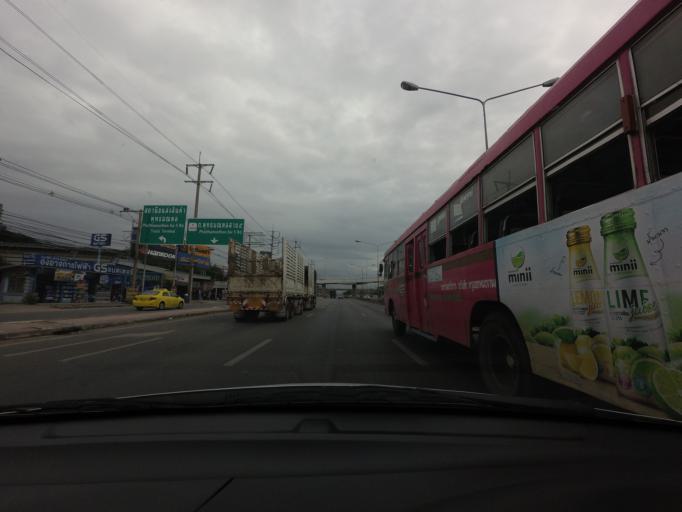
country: TH
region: Nakhon Pathom
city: Salaya
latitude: 13.7863
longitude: 100.2863
